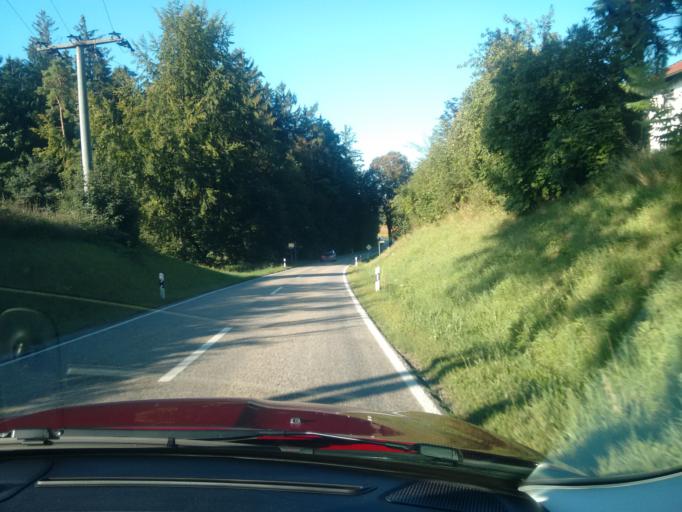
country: DE
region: Bavaria
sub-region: Upper Bavaria
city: Halsbach
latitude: 48.1225
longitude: 12.7189
